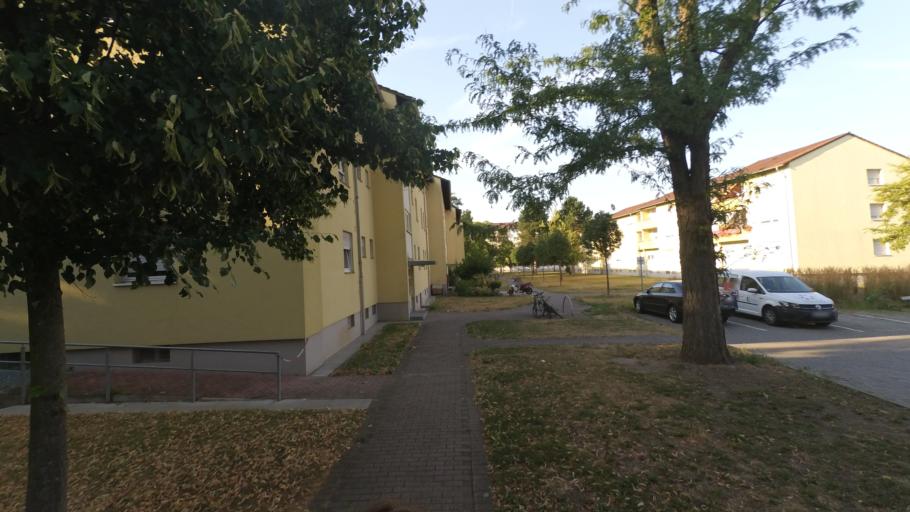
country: DE
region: Rheinland-Pfalz
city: Altrip
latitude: 49.4439
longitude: 8.5257
